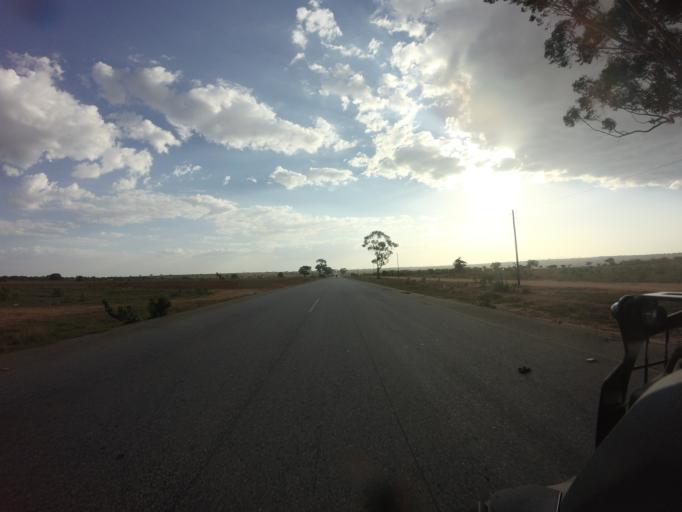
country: AO
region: Huila
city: Lubango
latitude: -14.7392
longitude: 13.8731
